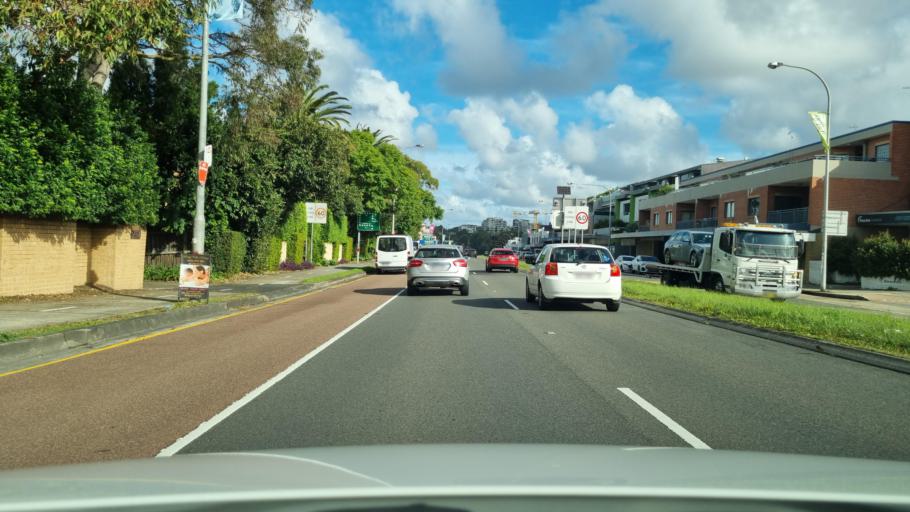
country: AU
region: New South Wales
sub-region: Warringah
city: North Manly
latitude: -33.7838
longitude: 151.2674
